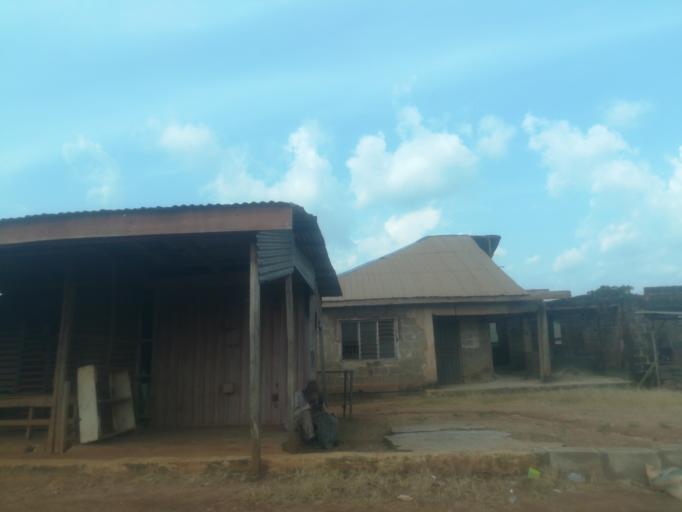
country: NG
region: Oyo
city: Ido
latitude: 7.3989
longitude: 3.8066
